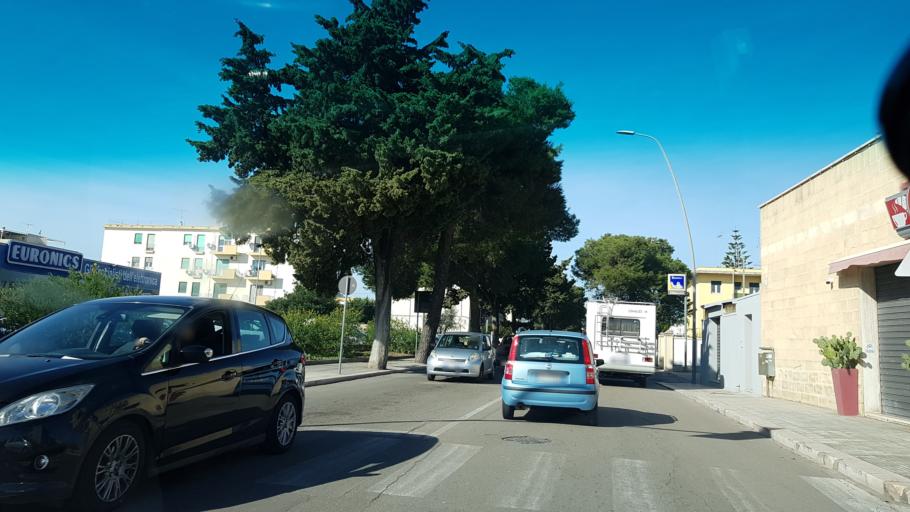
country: IT
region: Apulia
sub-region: Provincia di Lecce
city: Lecce
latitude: 40.3440
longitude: 18.1579
